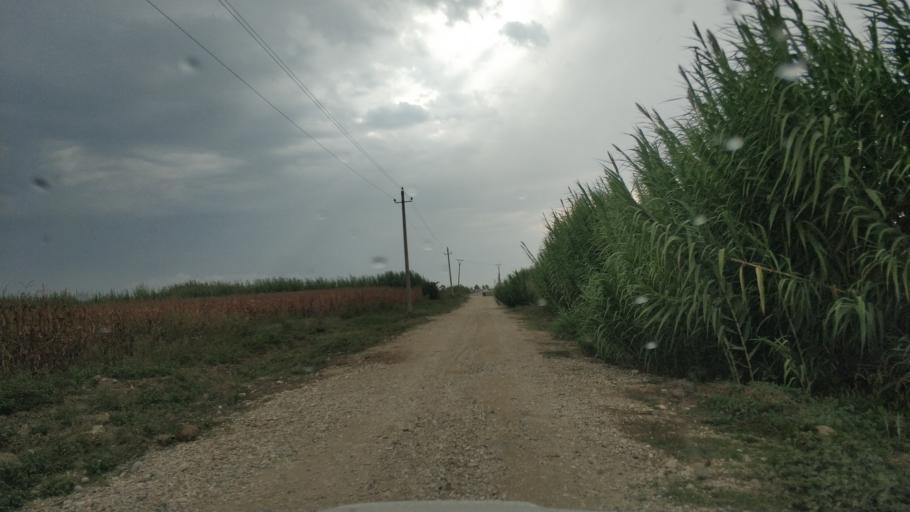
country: AL
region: Fier
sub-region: Rrethi i Fierit
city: Topoje
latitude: 40.7137
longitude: 19.4510
